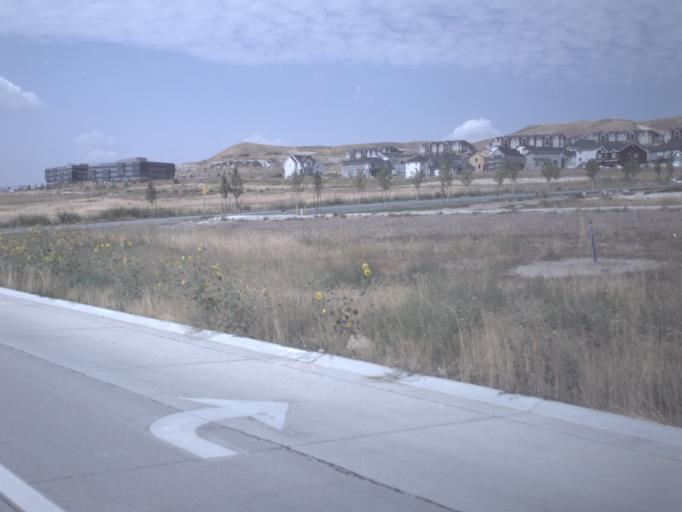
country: US
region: Utah
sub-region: Utah County
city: Lehi
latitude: 40.4326
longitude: -111.8598
